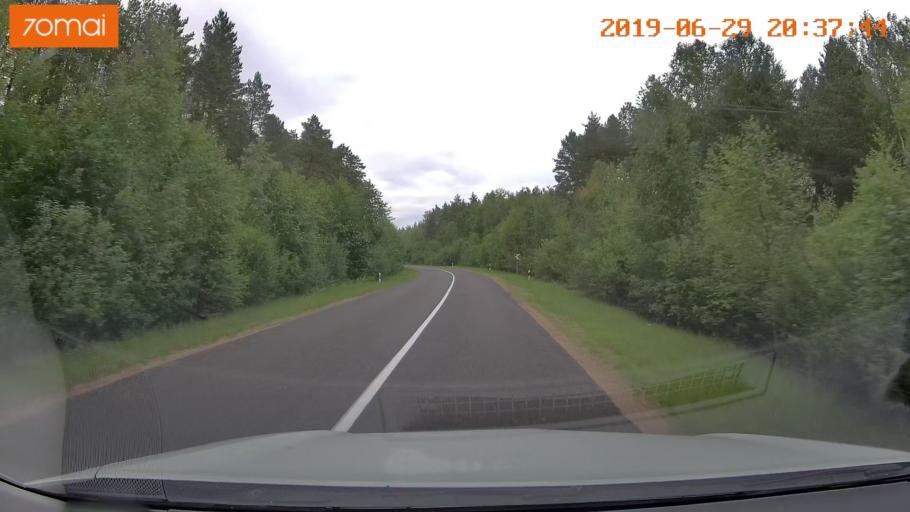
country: BY
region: Brest
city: Hantsavichy
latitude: 52.5419
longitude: 26.3656
